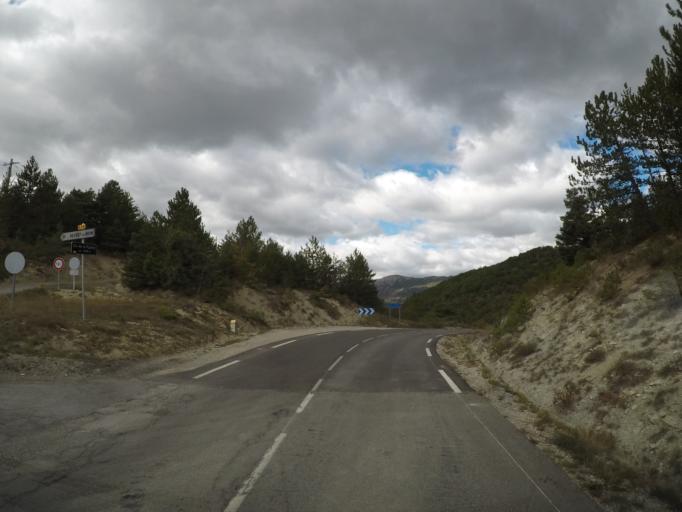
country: FR
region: Provence-Alpes-Cote d'Azur
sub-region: Departement du Vaucluse
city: Sault
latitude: 44.1796
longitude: 5.5685
